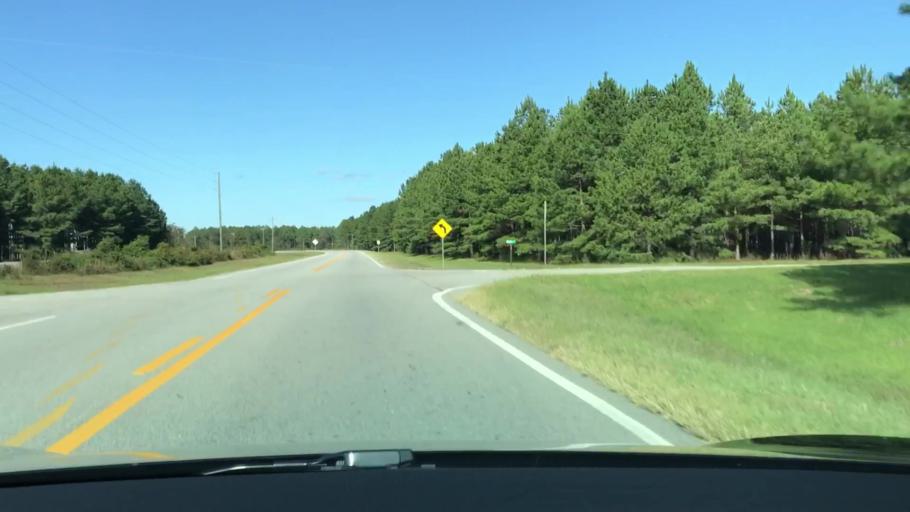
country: US
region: Georgia
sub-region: Glascock County
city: Gibson
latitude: 33.3029
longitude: -82.5219
